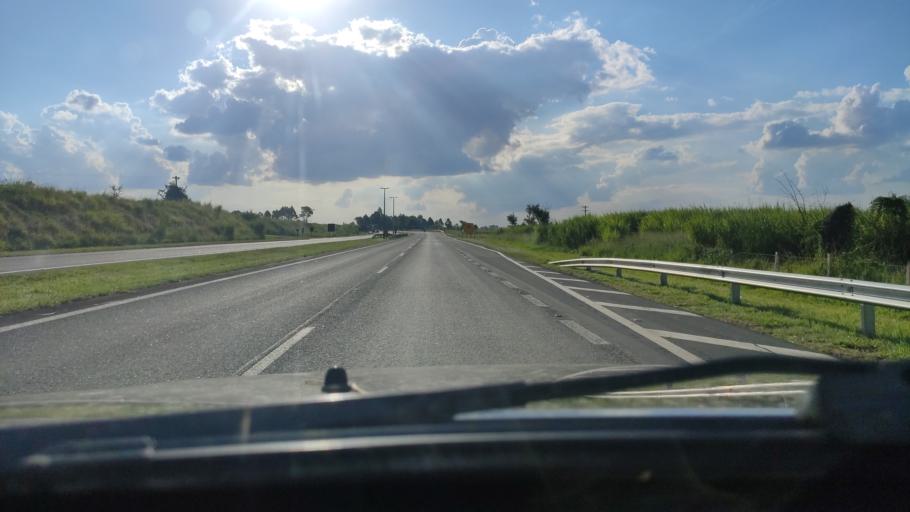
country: BR
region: Sao Paulo
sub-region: Itapira
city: Itapira
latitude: -22.4495
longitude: -46.8796
